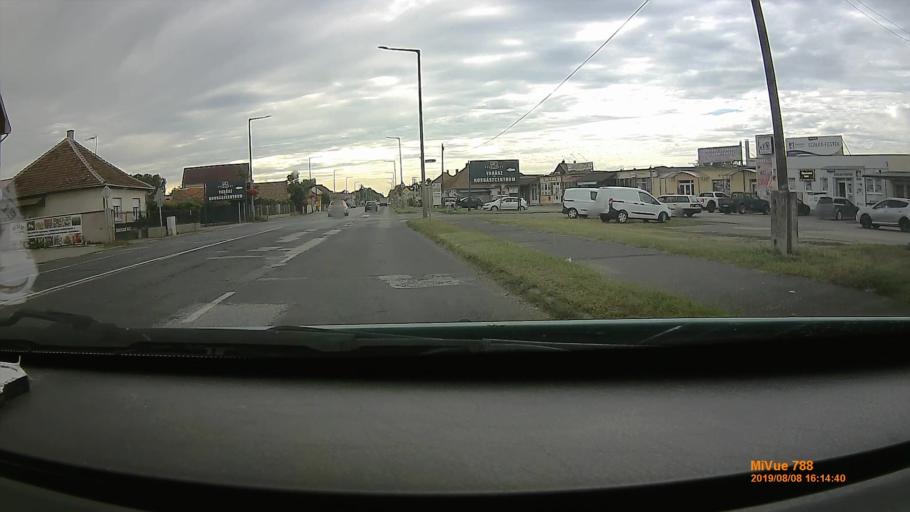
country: HU
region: Szabolcs-Szatmar-Bereg
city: Mateszalka
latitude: 47.9601
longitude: 22.3145
